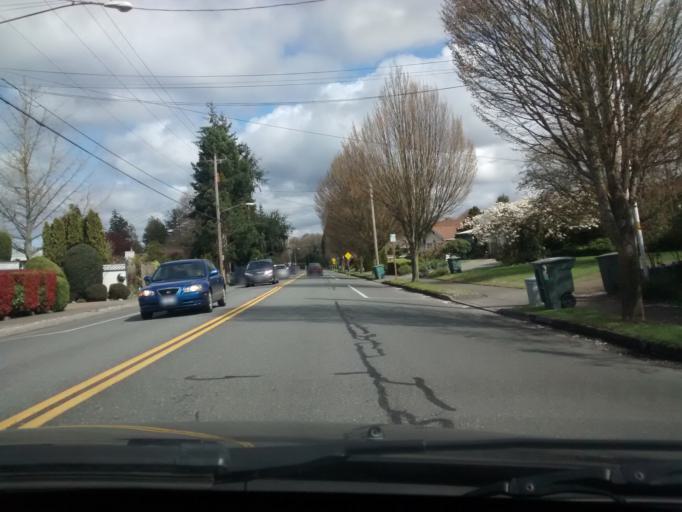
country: US
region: Washington
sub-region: Snohomish County
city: Edmonds
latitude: 47.8154
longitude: -122.3763
